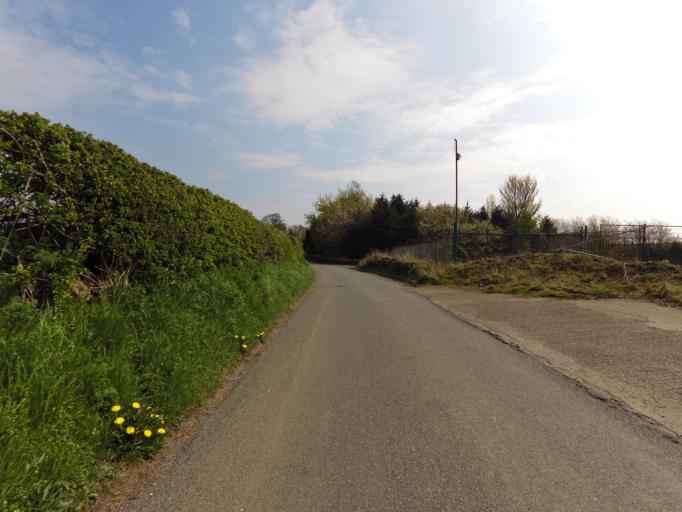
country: GB
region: Scotland
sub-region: Fife
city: Kinghorn
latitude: 56.0741
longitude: -3.1838
